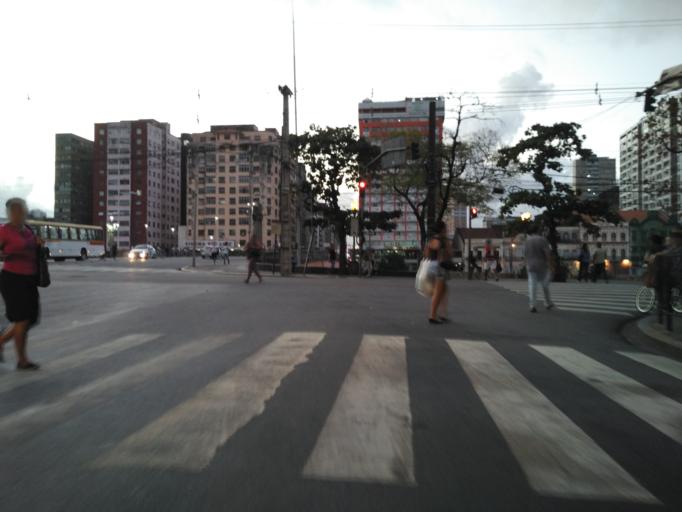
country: BR
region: Pernambuco
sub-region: Recife
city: Recife
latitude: -8.0626
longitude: -34.8801
